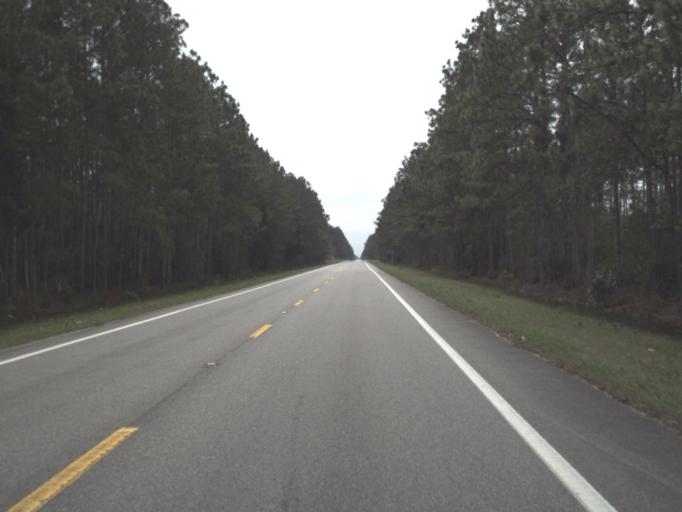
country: US
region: Florida
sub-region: Gulf County
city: Wewahitchka
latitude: 29.9423
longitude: -85.1865
